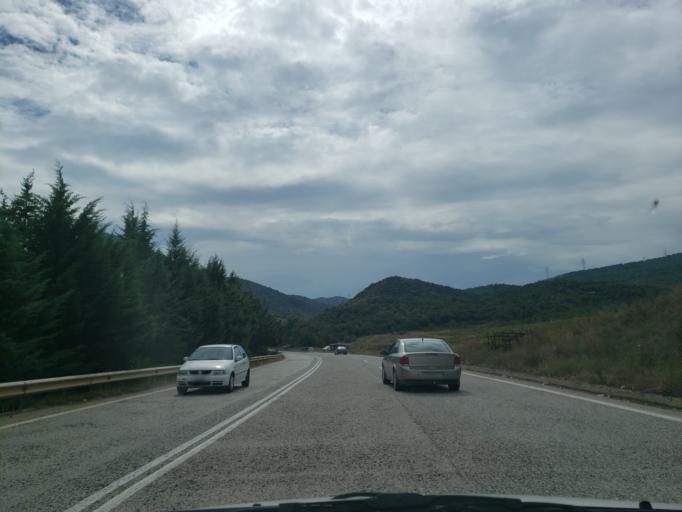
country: GR
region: Central Greece
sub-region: Nomos Fthiotidos
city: Stavros
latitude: 39.0170
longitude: 22.3763
